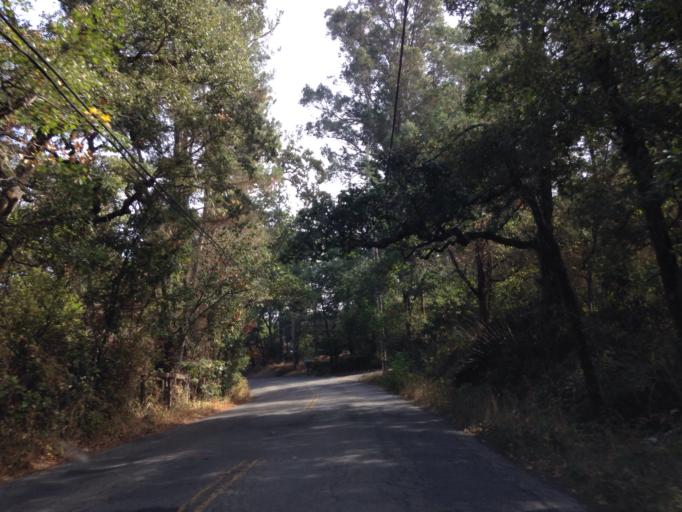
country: US
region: California
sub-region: Sonoma County
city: Graton
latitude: 38.4349
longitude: -122.8857
